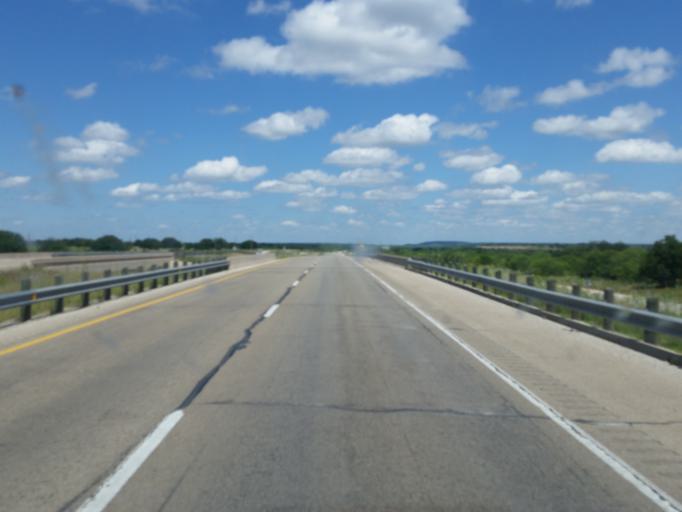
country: US
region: Texas
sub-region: Callahan County
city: Baird
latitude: 32.3859
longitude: -99.2993
